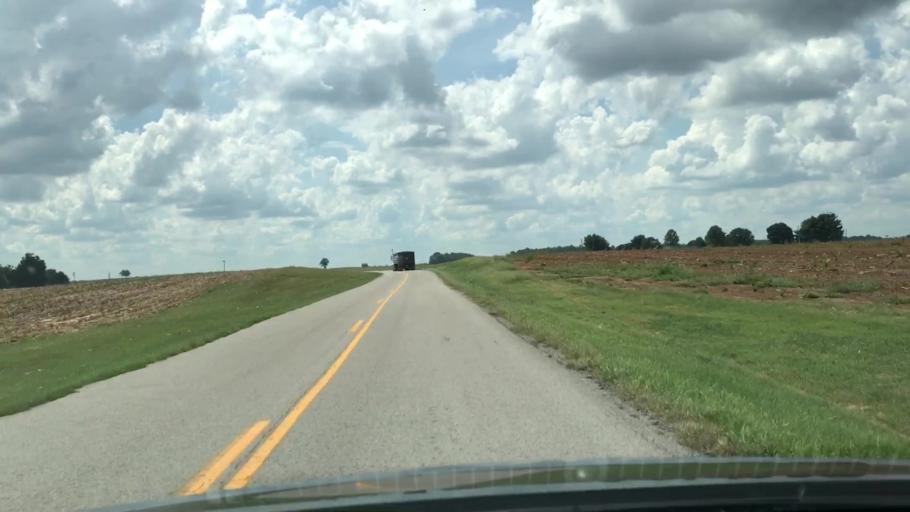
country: US
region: Kentucky
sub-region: Todd County
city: Guthrie
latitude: 36.6605
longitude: -87.0266
